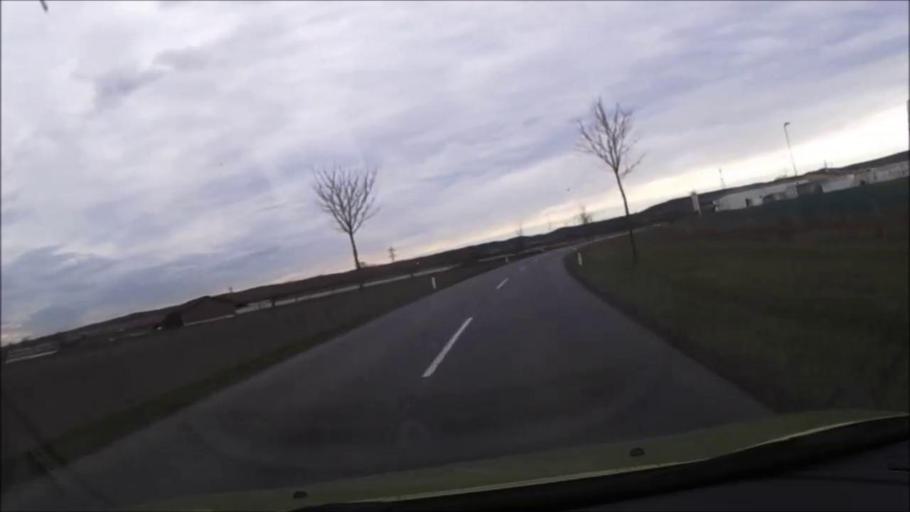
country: AT
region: Burgenland
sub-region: Eisenstadt-Umgebung
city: Leithaprodersdorf
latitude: 47.9340
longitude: 16.4916
